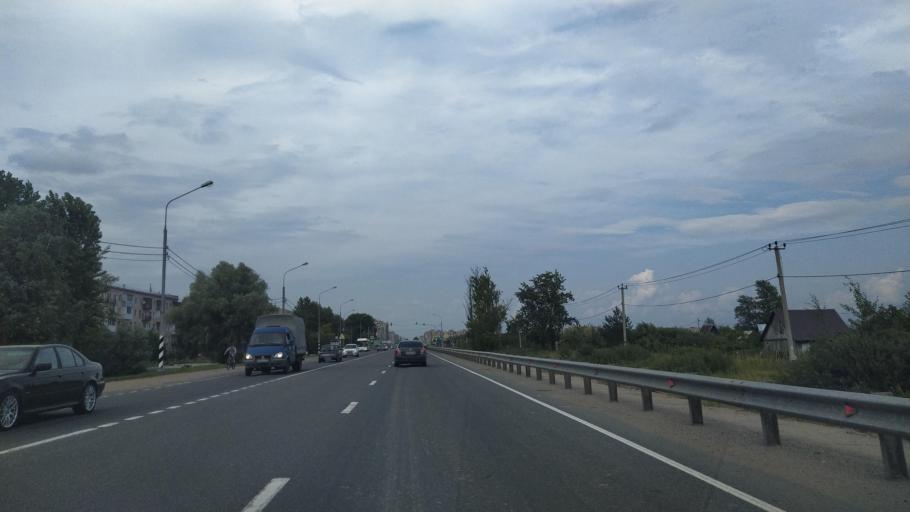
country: RU
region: Novgorod
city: Pankovka
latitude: 58.4978
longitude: 31.2145
